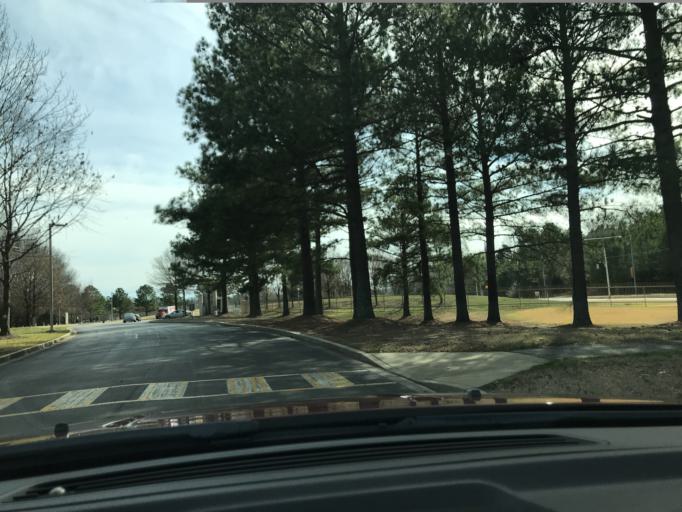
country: US
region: Tennessee
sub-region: Shelby County
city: Collierville
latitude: 35.0372
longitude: -89.7237
